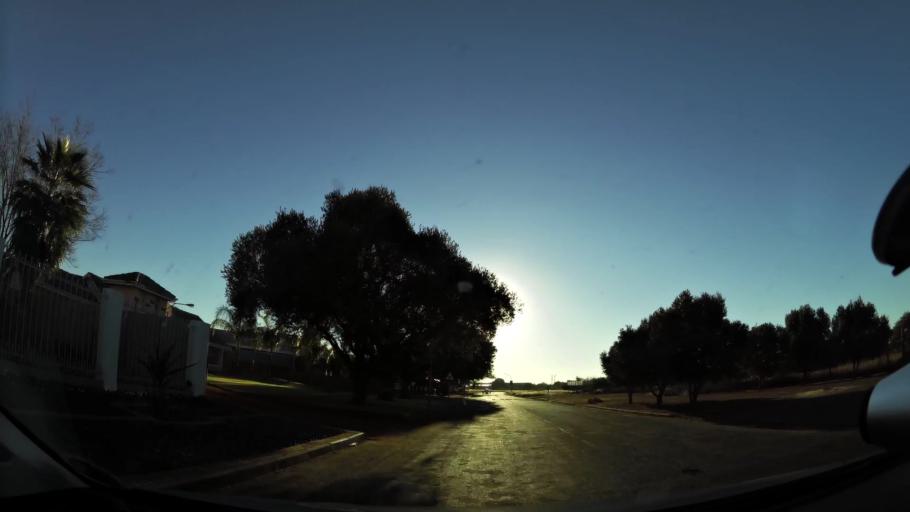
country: ZA
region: Northern Cape
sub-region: Frances Baard District Municipality
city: Kimberley
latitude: -28.7583
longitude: 24.7477
